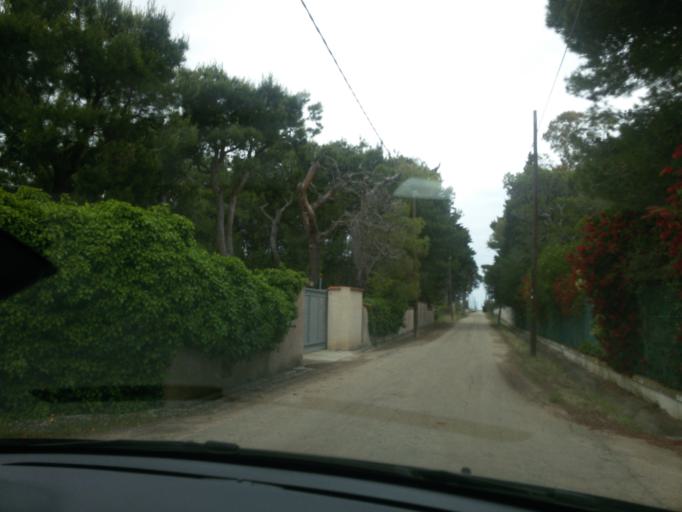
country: IT
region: Apulia
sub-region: Provincia di Brindisi
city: Brindisi
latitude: 40.6353
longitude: 17.8969
